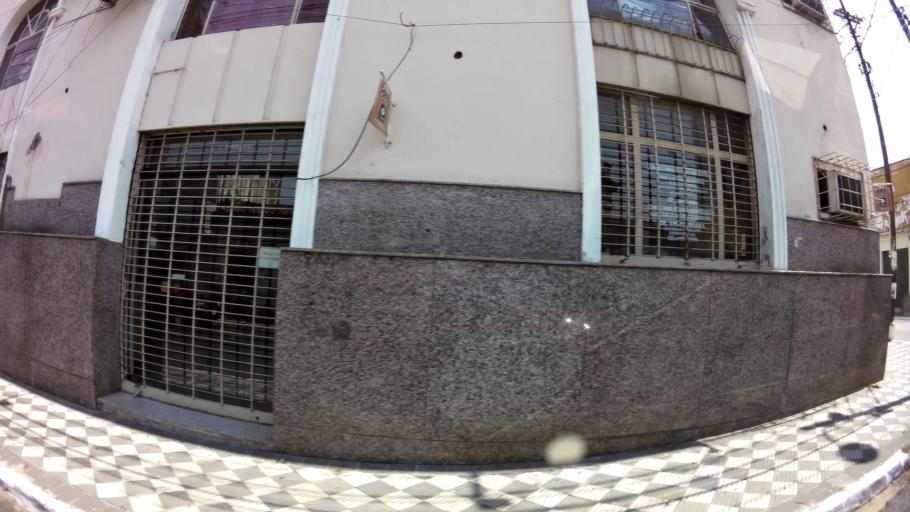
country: PY
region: Asuncion
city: Asuncion
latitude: -25.2796
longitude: -57.6438
